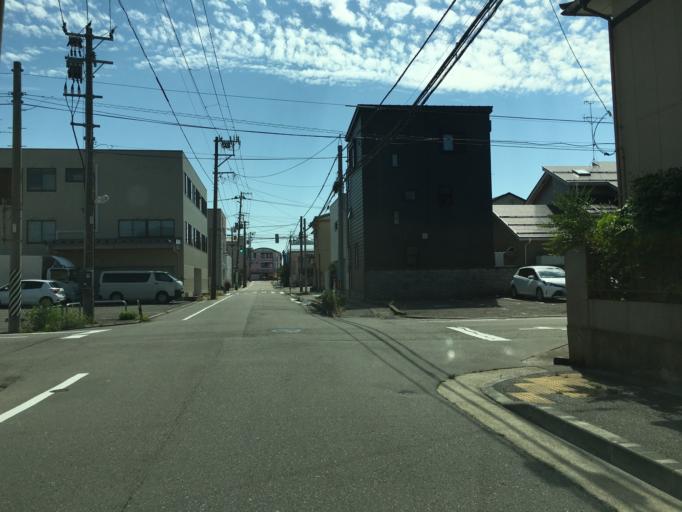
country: JP
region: Niigata
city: Niigata-shi
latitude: 37.9116
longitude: 139.0244
